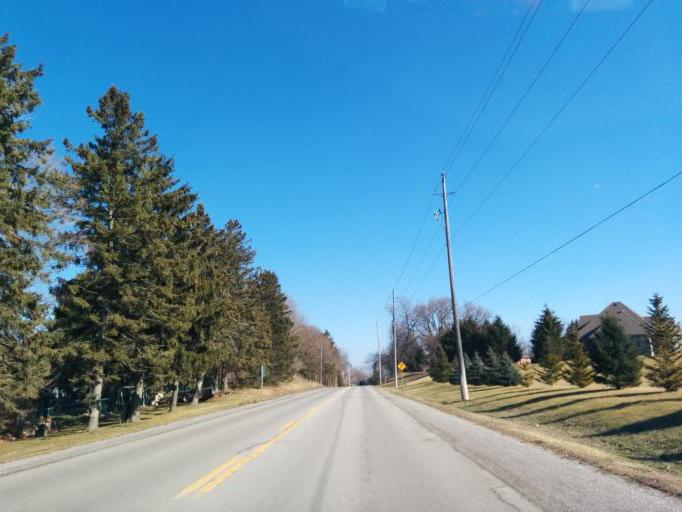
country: CA
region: Ontario
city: Norfolk County
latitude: 42.8327
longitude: -80.3247
